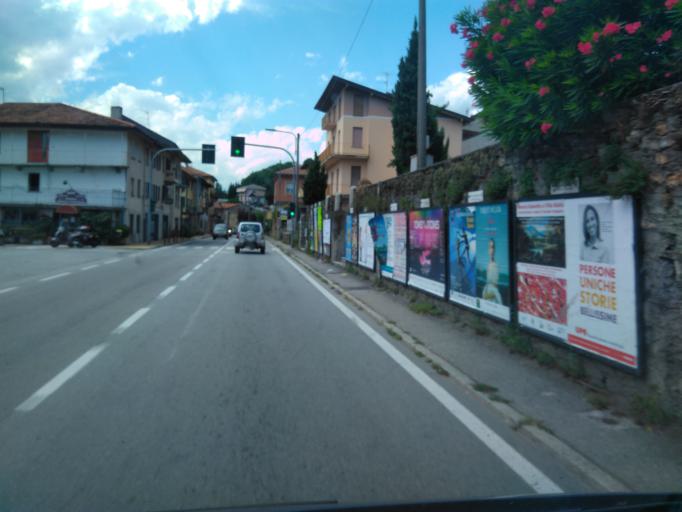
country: IT
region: Piedmont
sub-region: Provincia Verbano-Cusio-Ossola
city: Cossogno
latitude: 45.9450
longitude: 8.4971
